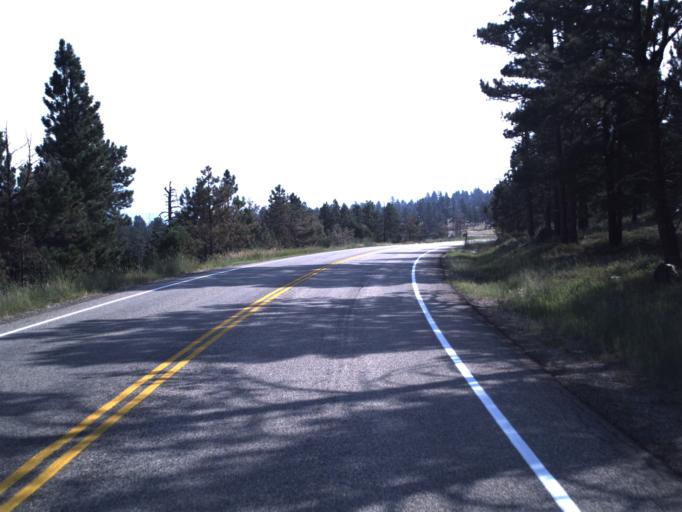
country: US
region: Utah
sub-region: Daggett County
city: Manila
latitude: 40.8715
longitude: -109.4703
